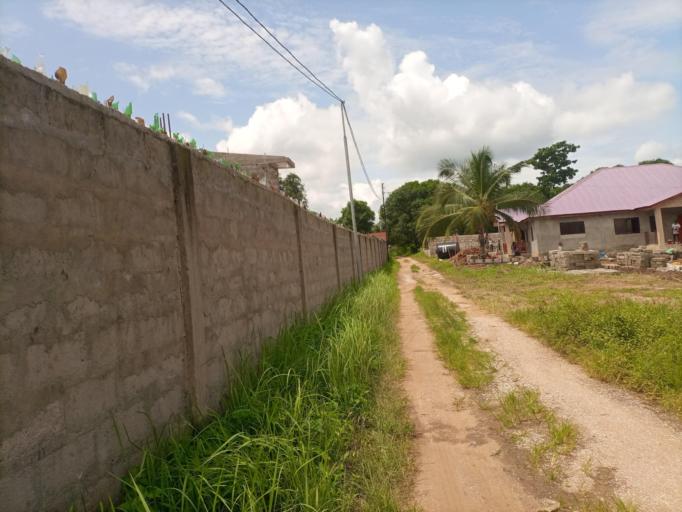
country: SL
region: Northern Province
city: Masoyila
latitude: 8.5419
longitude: -13.1520
